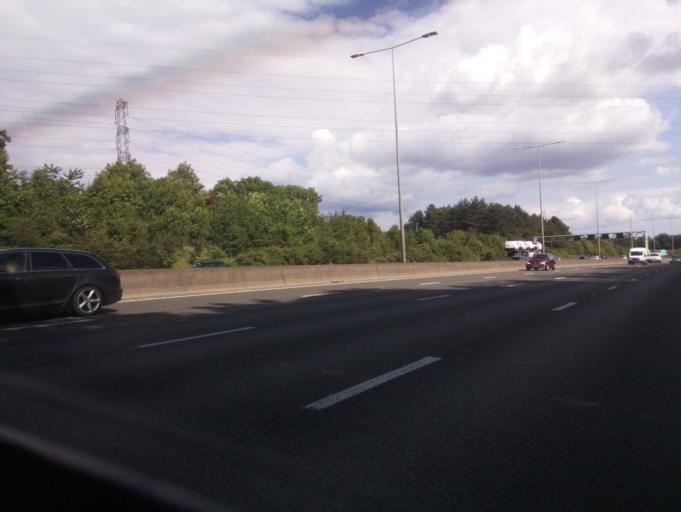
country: GB
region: England
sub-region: Hertfordshire
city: Abbots Langley
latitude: 51.7408
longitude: -0.3997
